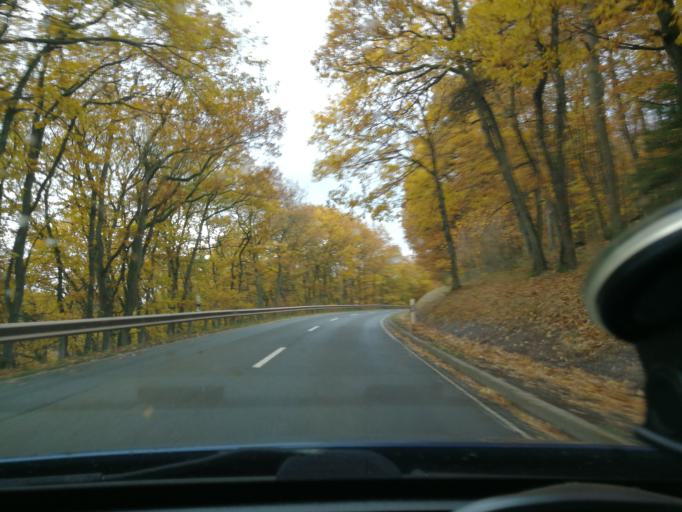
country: DE
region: Rheinland-Pfalz
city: Klausen
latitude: 49.8949
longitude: 6.8933
